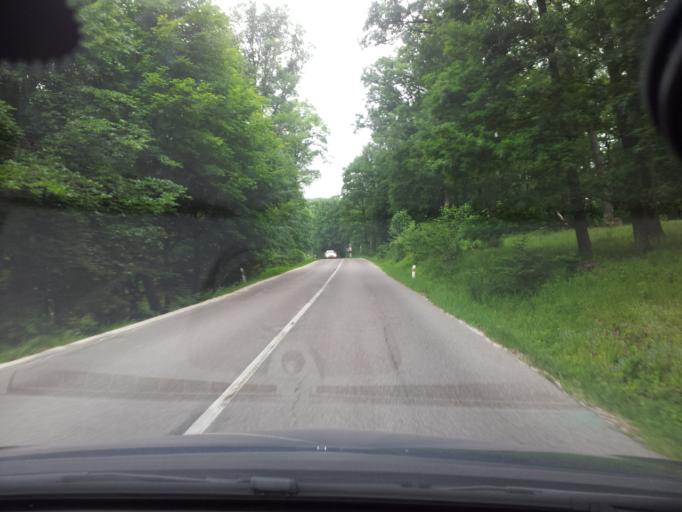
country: SK
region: Nitriansky
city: Partizanske
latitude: 48.5482
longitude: 18.4390
